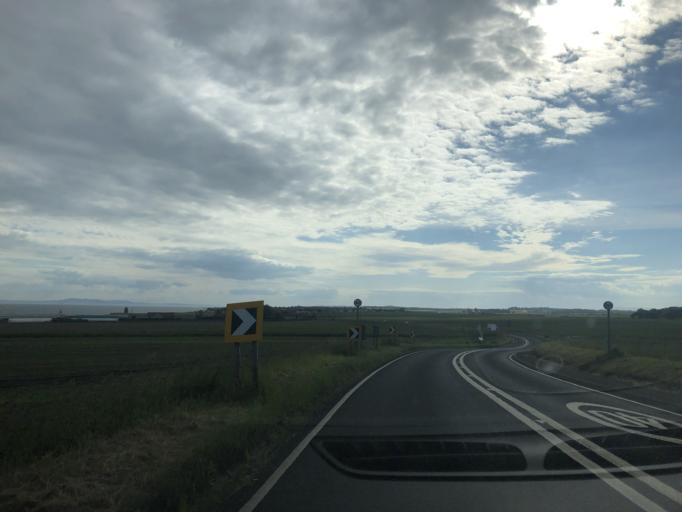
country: GB
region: Scotland
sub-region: Fife
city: Pittenweem
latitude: 56.2132
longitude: -2.7433
